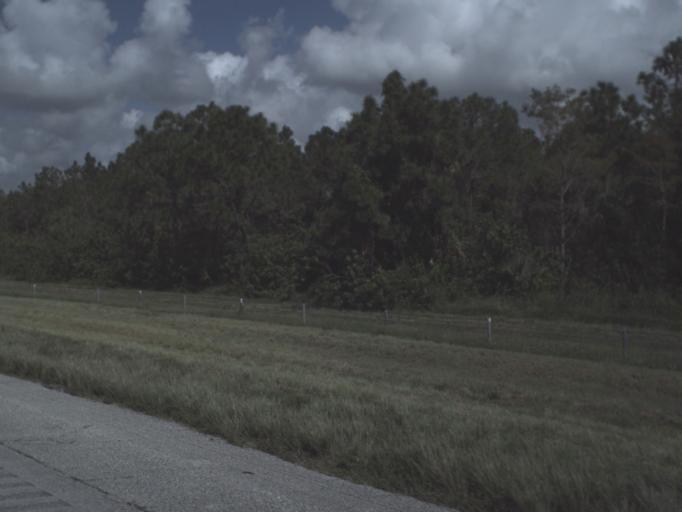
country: US
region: Florida
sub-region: Indian River County
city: West Vero Corridor
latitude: 27.5446
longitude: -80.6250
